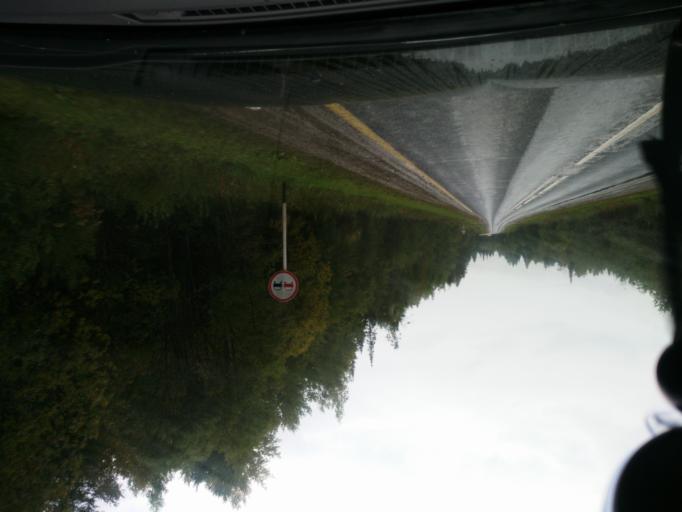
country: RU
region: Perm
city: Yugo-Kamskiy
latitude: 57.5228
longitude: 55.6847
